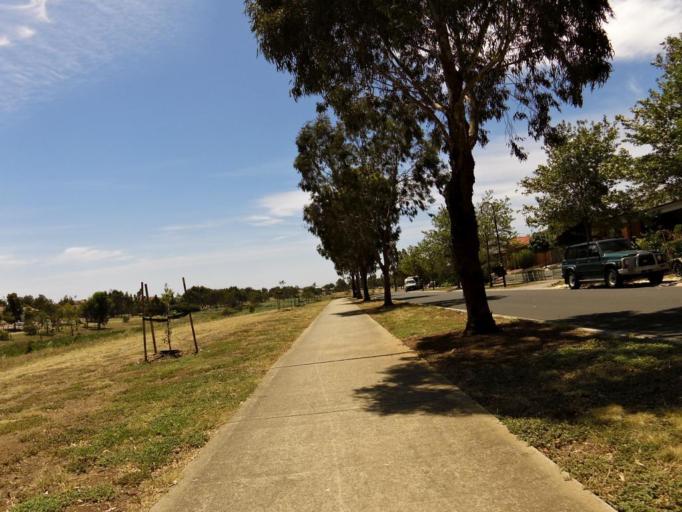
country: AU
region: Victoria
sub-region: Wyndham
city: Williams Landing
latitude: -37.8569
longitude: 144.7150
